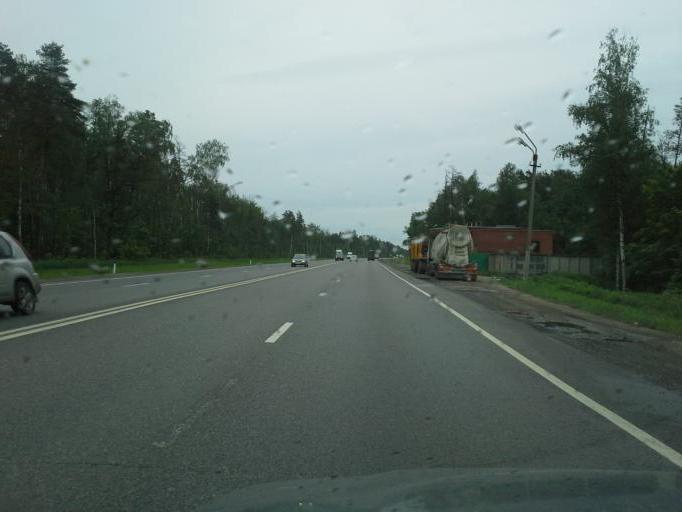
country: RU
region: Vladimir
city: Pokrov
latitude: 55.9059
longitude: 39.0994
